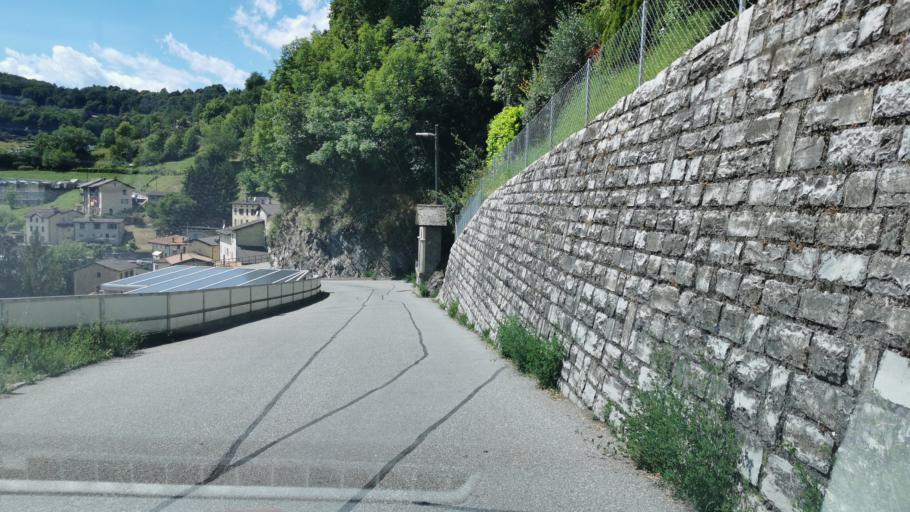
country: IT
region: Lombardy
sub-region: Provincia di Como
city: Campione
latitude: 45.9601
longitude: 8.9933
